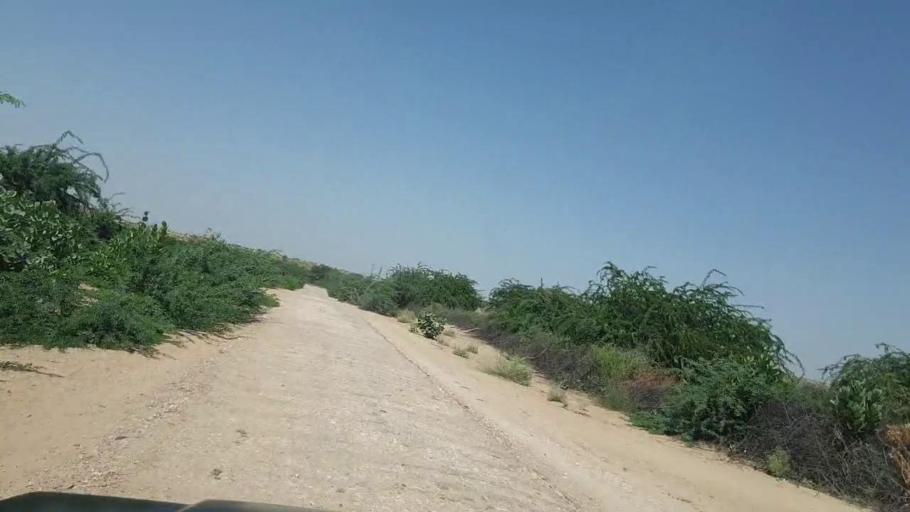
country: PK
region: Sindh
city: Chor
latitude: 25.4068
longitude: 70.3080
